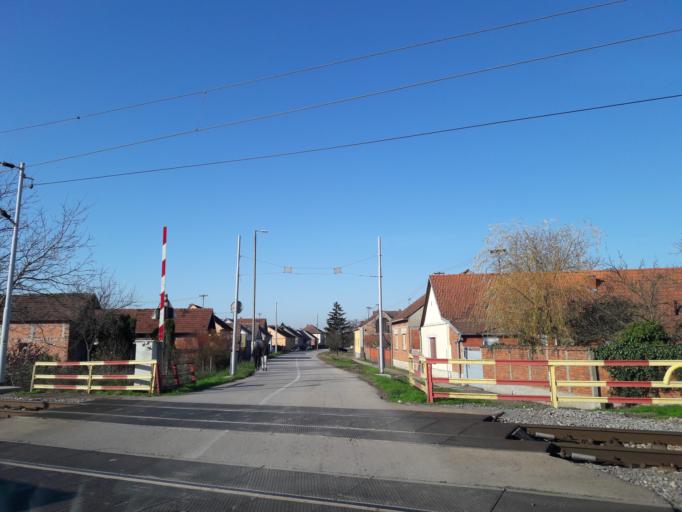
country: HR
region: Vukovarsko-Srijemska
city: Vodinci
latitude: 45.2696
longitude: 18.6135
